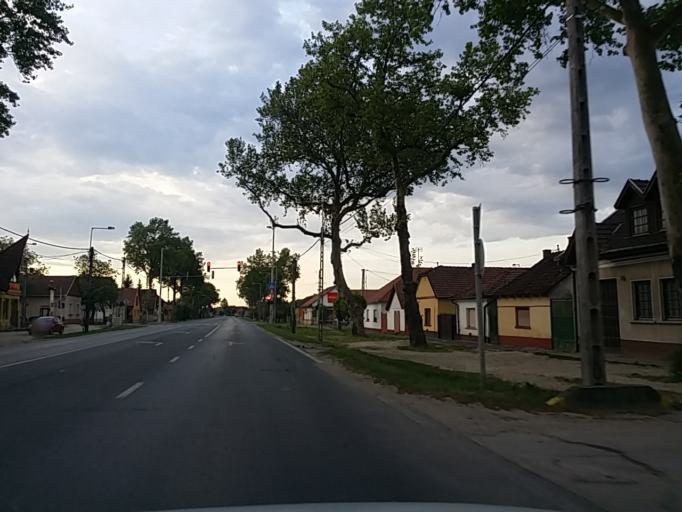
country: HU
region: Bacs-Kiskun
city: Lajosmizse
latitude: 47.0227
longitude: 19.5627
